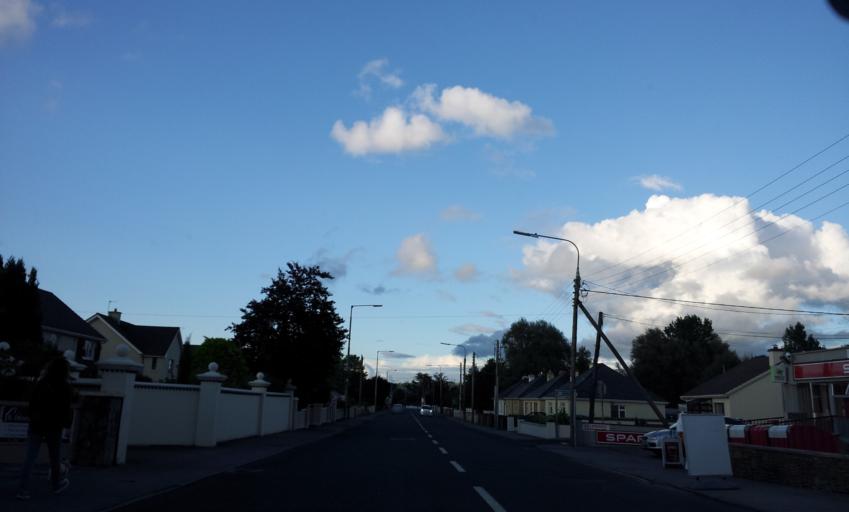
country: IE
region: Munster
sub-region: County Limerick
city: Abbeyfeale
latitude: 52.3787
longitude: -9.3049
